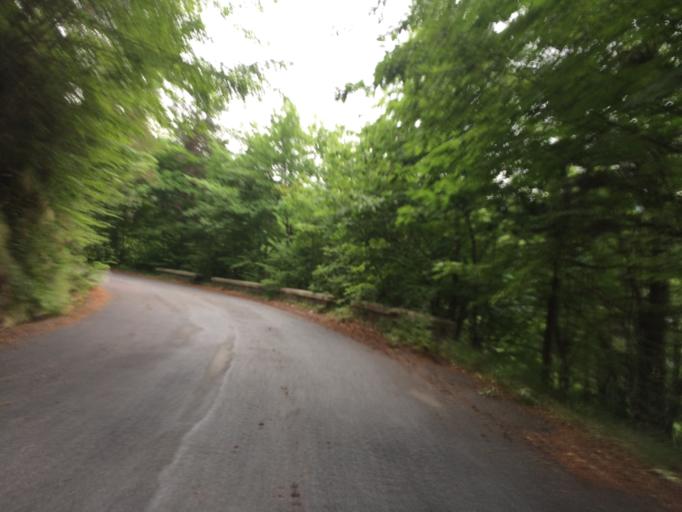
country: IT
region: Liguria
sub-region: Provincia di Imperia
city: Triora
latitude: 43.9701
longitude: 7.7447
